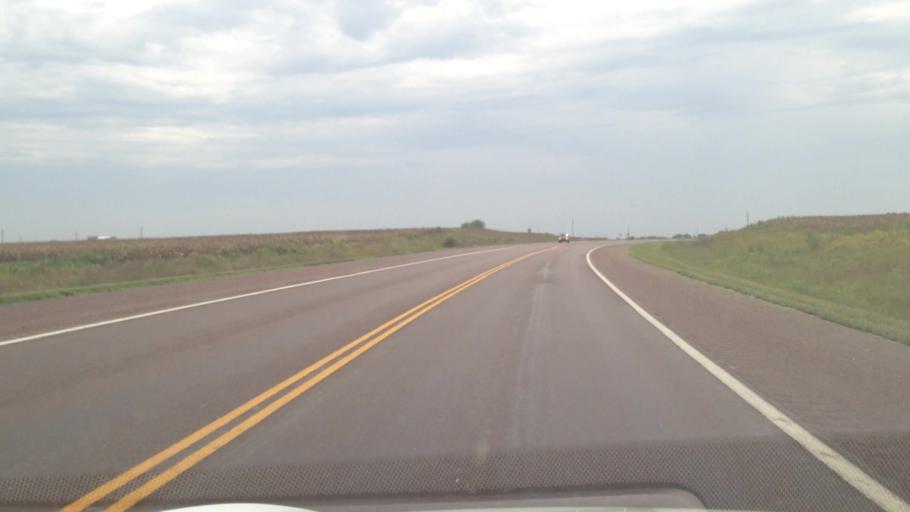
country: US
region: Kansas
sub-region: Crawford County
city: Girard
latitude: 37.4730
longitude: -94.8366
